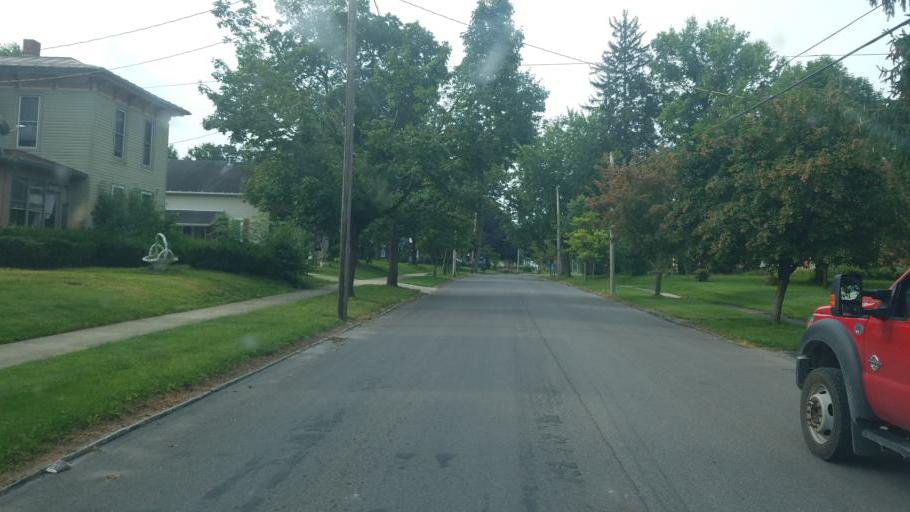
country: US
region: Ohio
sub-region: Morrow County
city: Cardington
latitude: 40.4964
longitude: -82.8940
